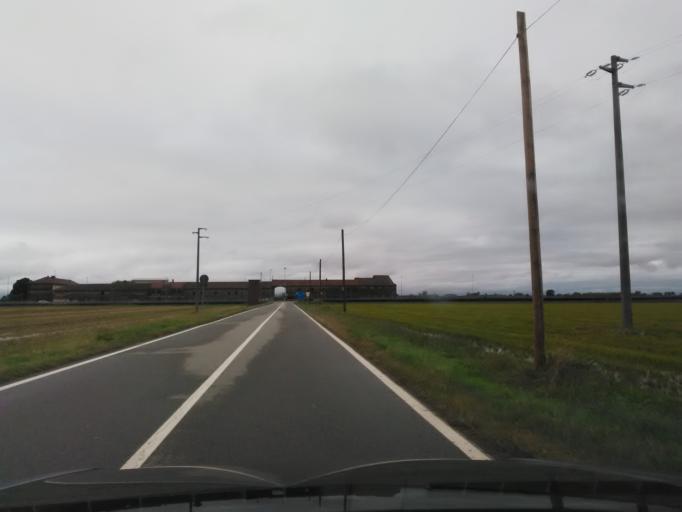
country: IT
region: Piedmont
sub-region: Provincia di Vercelli
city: Olcenengo
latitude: 45.3425
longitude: 8.2893
